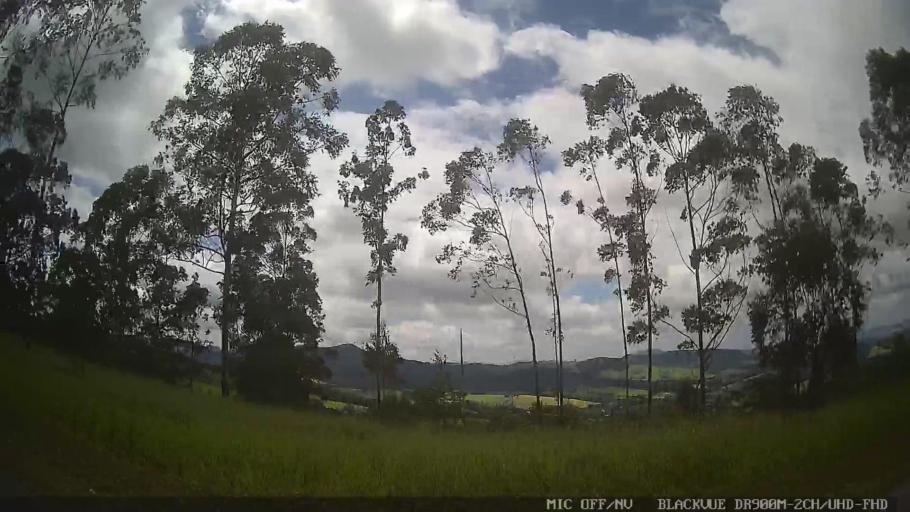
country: BR
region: Sao Paulo
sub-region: Braganca Paulista
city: Braganca Paulista
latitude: -22.8100
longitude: -46.5383
